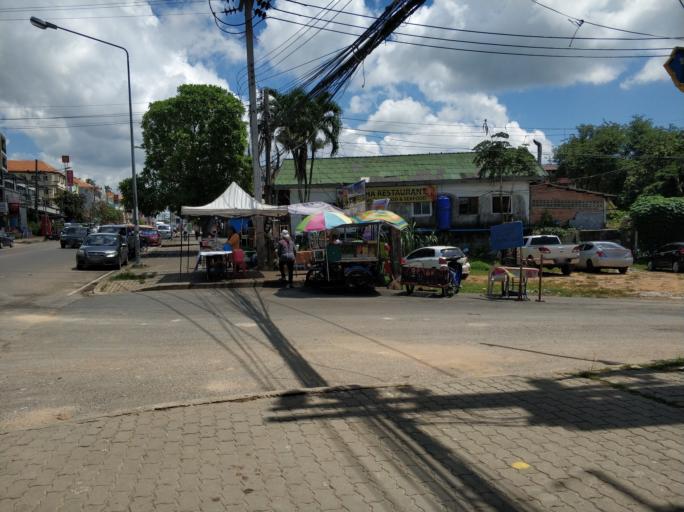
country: TH
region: Phangnga
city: Ban Ao Nang
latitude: 8.0336
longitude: 98.8282
